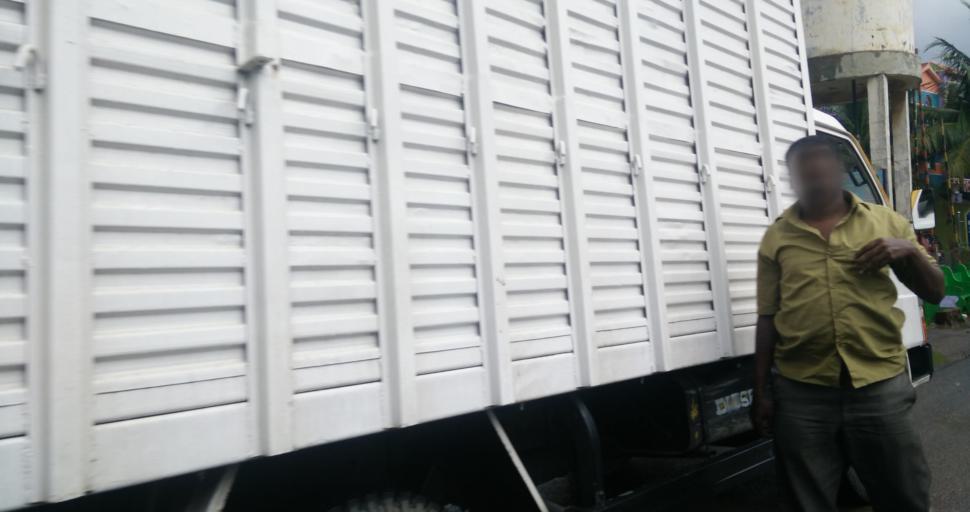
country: IN
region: Tamil Nadu
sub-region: Kancheepuram
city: Nandambakkam
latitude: 12.9820
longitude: 80.0153
